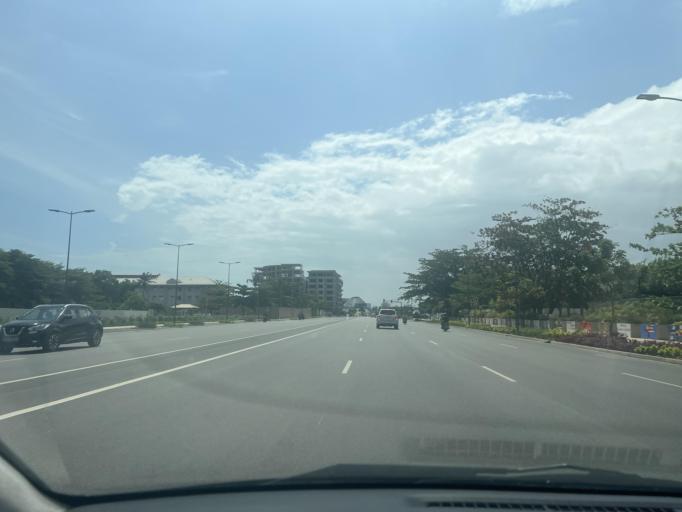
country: BJ
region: Littoral
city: Cotonou
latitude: 6.3501
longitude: 2.4031
